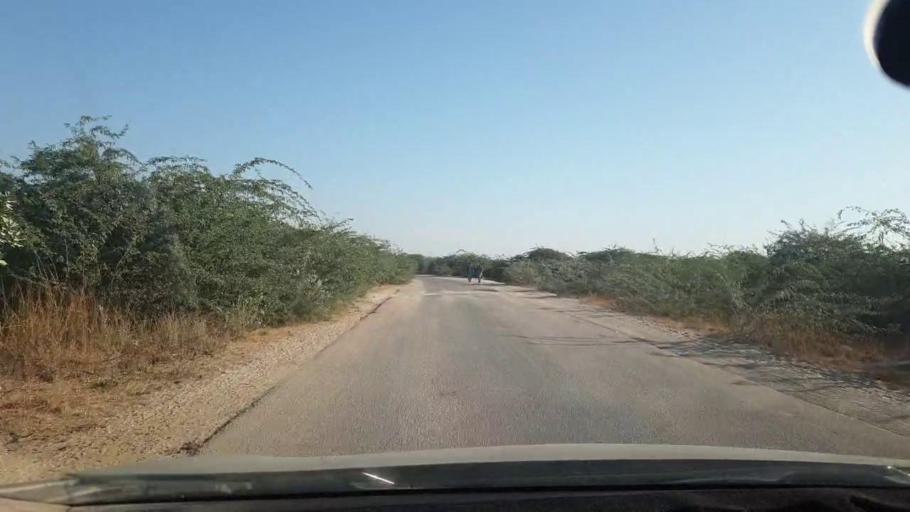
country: PK
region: Sindh
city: Malir Cantonment
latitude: 25.1694
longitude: 67.1998
